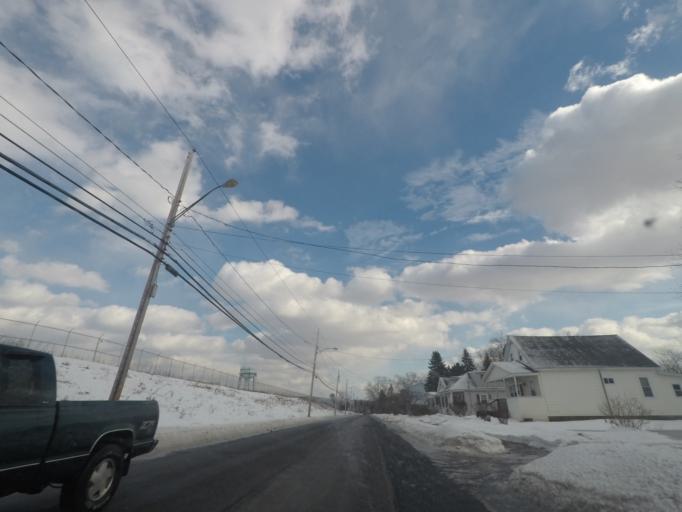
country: US
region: New York
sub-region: Albany County
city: Cohoes
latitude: 42.7792
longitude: -73.7262
